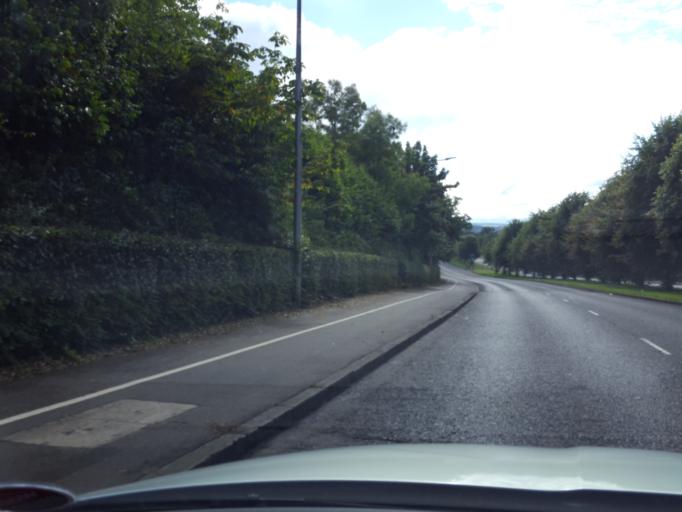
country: GB
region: Scotland
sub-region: Fife
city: Rosyth
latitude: 56.0571
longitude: -3.4409
